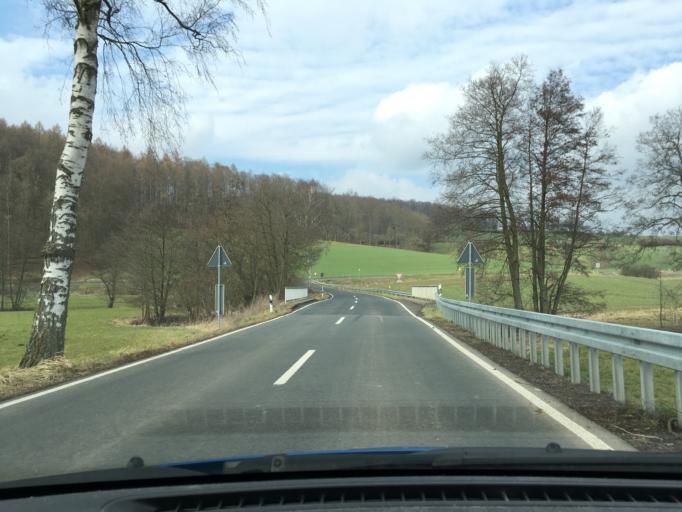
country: DE
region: Lower Saxony
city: Adelebsen
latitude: 51.5724
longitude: 9.7195
